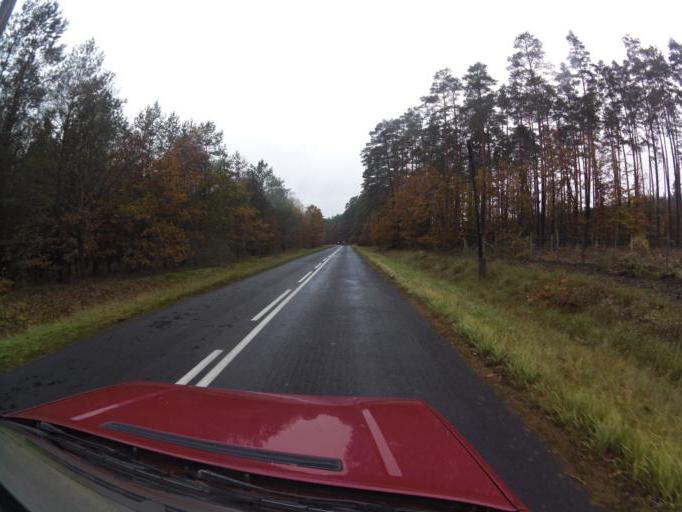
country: PL
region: West Pomeranian Voivodeship
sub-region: Powiat policki
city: Dobra
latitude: 53.5883
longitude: 14.3730
